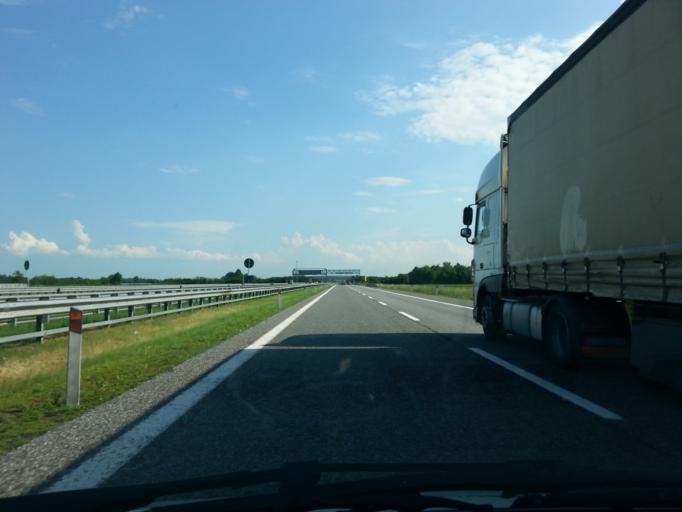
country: IT
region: Piedmont
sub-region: Provincia di Torino
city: Carmagnola
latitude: 44.8438
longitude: 7.7491
